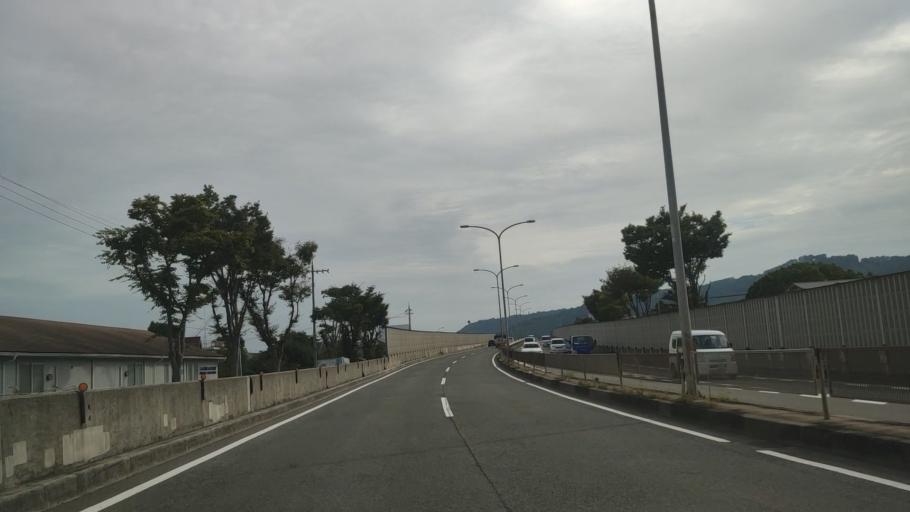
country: JP
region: Osaka
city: Tondabayashicho
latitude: 34.4577
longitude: 135.5661
